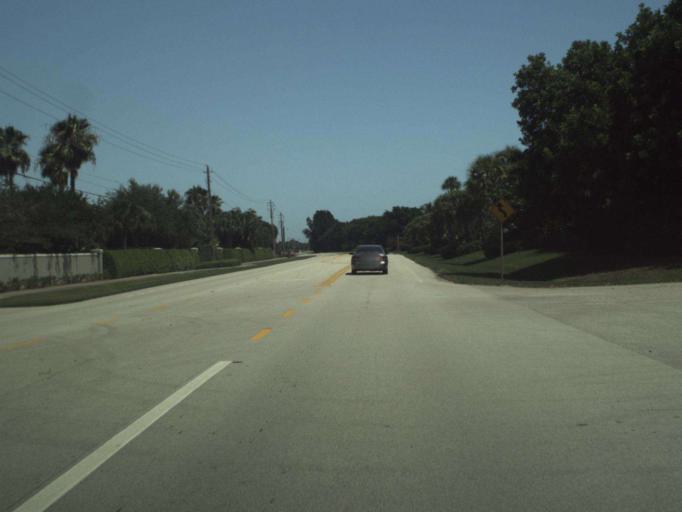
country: US
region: Florida
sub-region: Indian River County
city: South Beach
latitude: 27.5806
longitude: -80.3305
